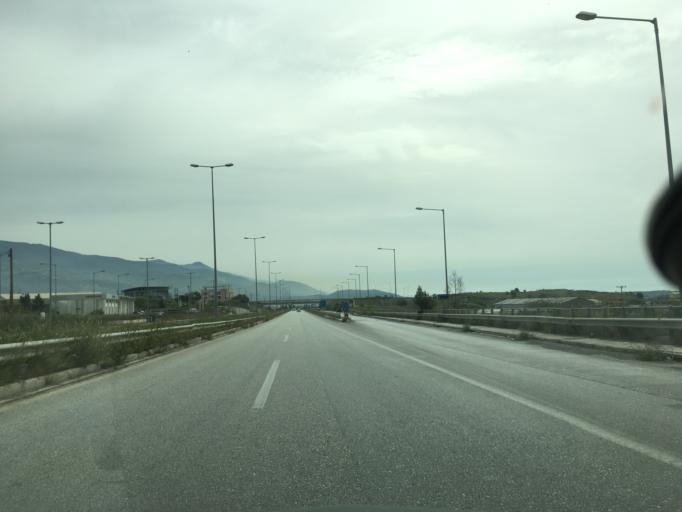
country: GR
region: Thessaly
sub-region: Nomos Magnisias
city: Nea Ionia
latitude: 39.3752
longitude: 22.8978
